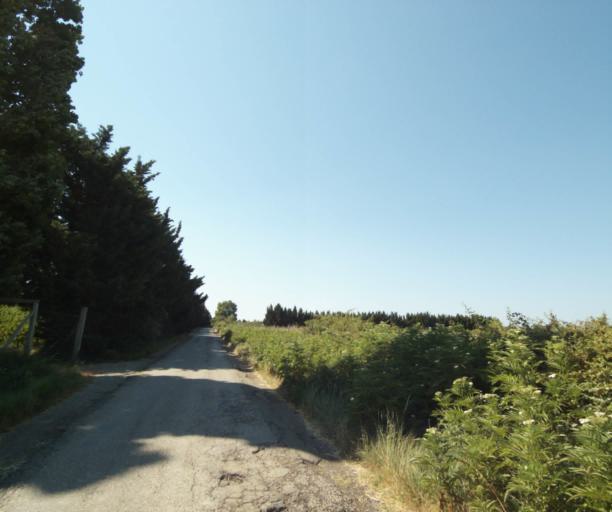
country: FR
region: Languedoc-Roussillon
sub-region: Departement de l'Herault
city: Marsillargues
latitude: 43.6540
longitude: 4.1657
